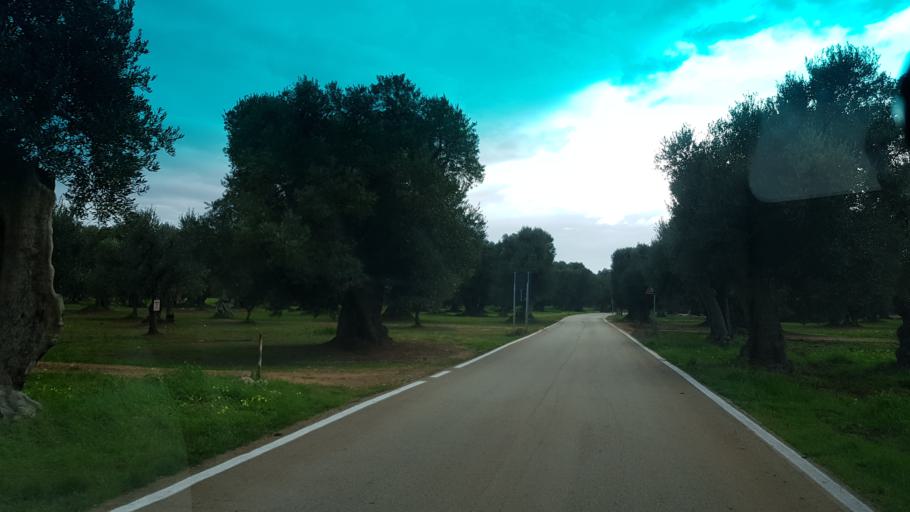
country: IT
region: Apulia
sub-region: Provincia di Brindisi
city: San Vito dei Normanni
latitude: 40.7039
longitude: 17.7636
